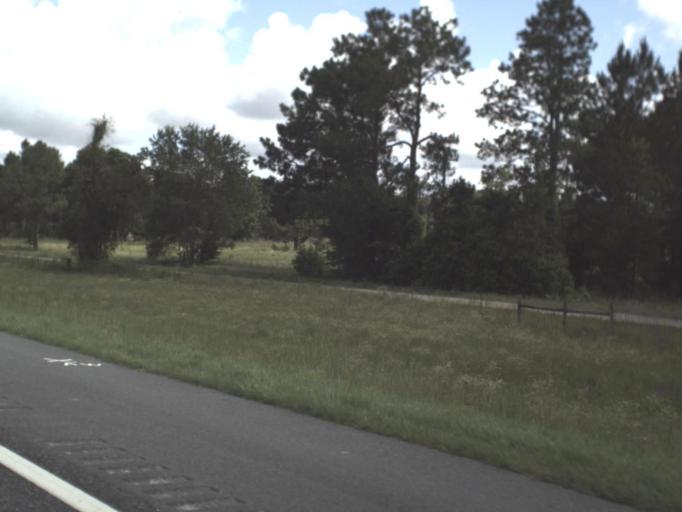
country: US
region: Florida
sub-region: Alachua County
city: High Springs
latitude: 29.9946
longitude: -82.5869
